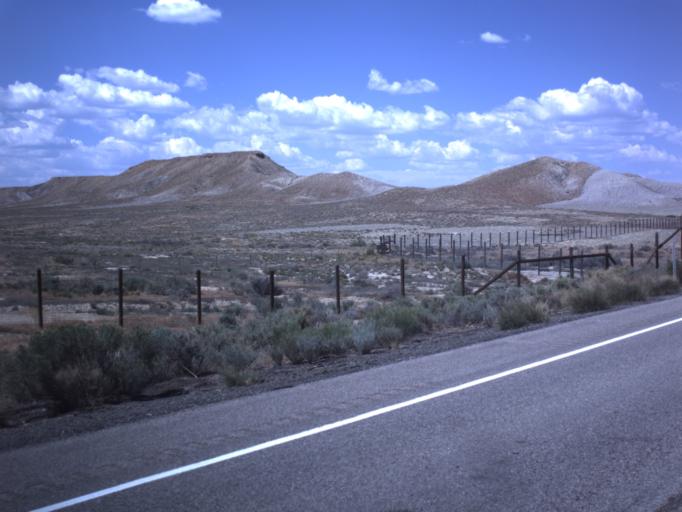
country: US
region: Utah
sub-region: Emery County
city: Huntington
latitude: 39.4127
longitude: -110.8781
